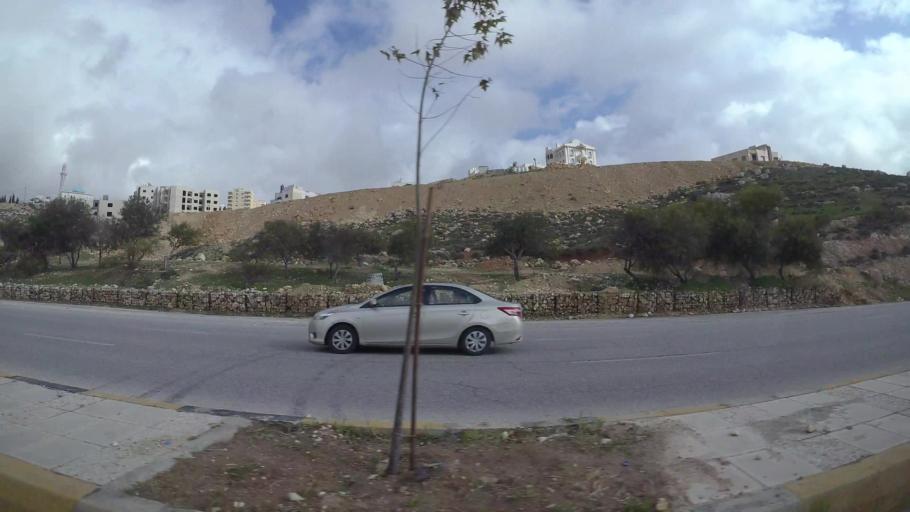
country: JO
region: Amman
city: Al Jubayhah
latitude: 32.0688
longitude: 35.8736
